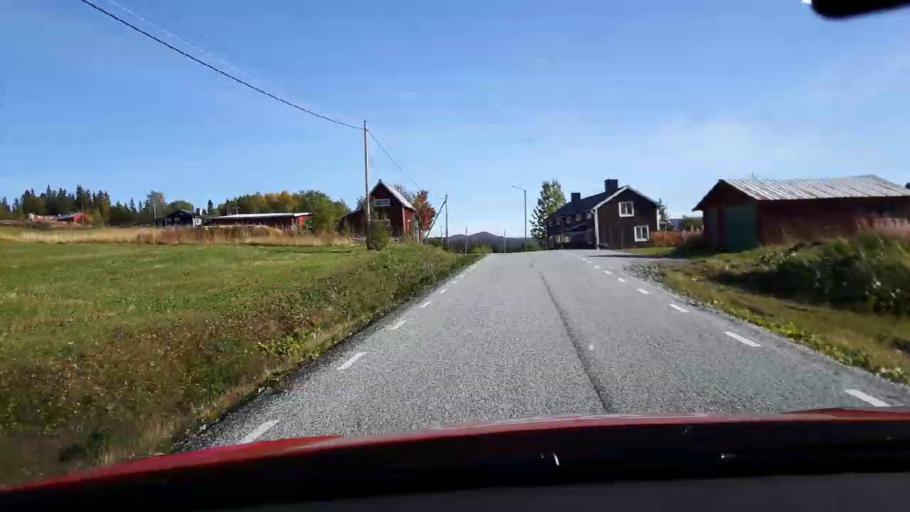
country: NO
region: Nord-Trondelag
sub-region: Royrvik
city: Royrvik
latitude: 64.8122
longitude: 14.1626
